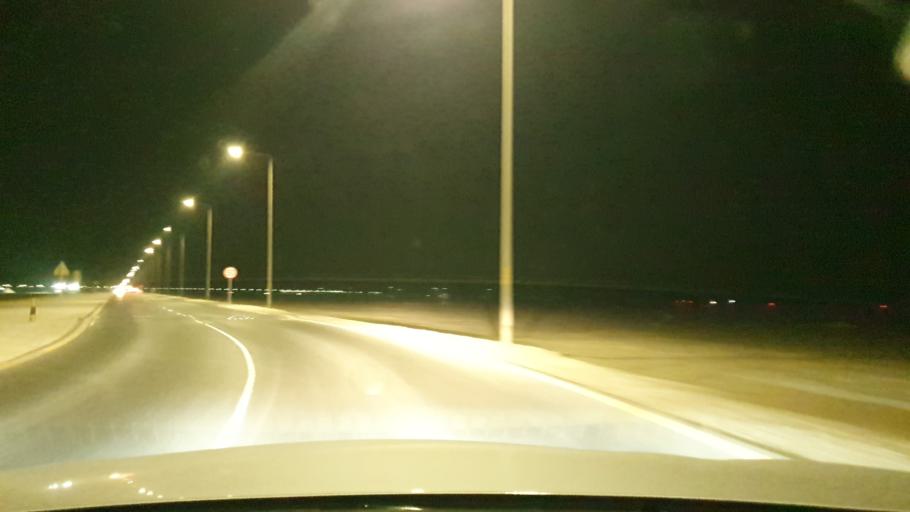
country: BH
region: Muharraq
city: Al Muharraq
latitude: 26.2789
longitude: 50.5938
